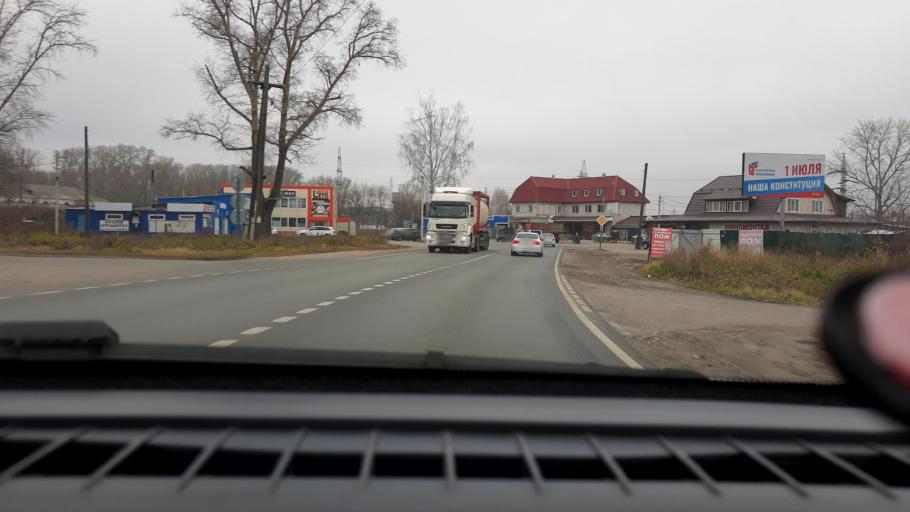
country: RU
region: Nizjnij Novgorod
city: Novaya Balakhna
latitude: 56.4988
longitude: 43.5939
